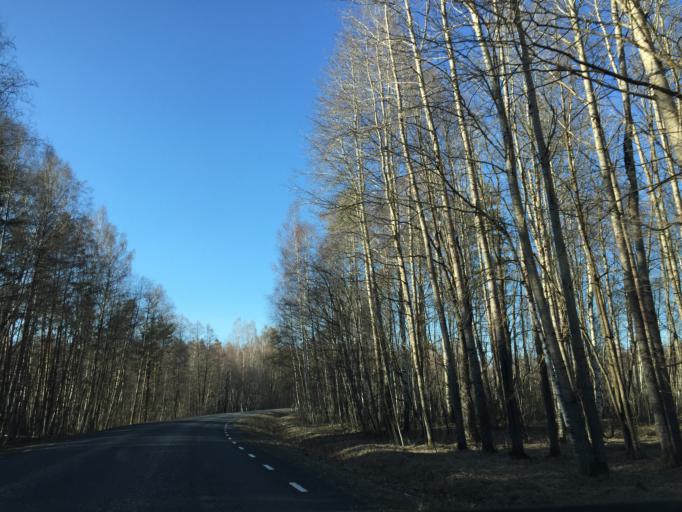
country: RU
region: Pskov
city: Gdov
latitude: 59.0243
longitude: 27.6867
